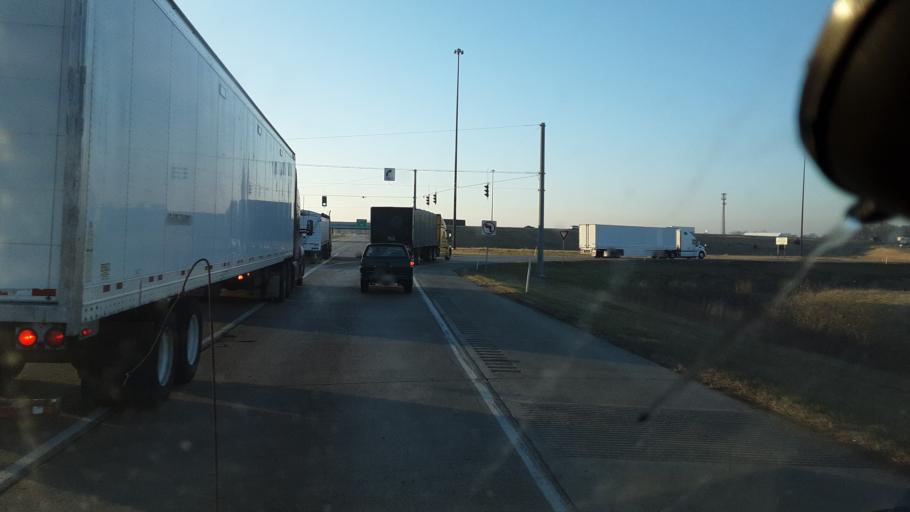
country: US
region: Indiana
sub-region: Allen County
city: New Haven
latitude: 41.0625
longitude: -84.9858
